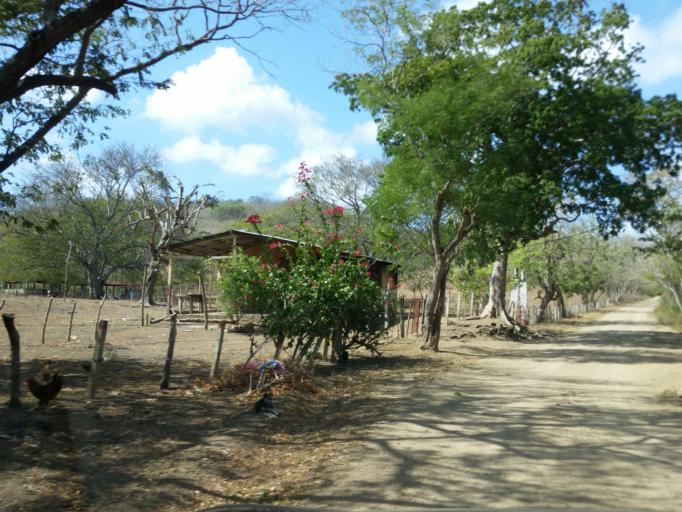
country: CR
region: Guanacaste
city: La Cruz
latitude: 11.1085
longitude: -85.7431
